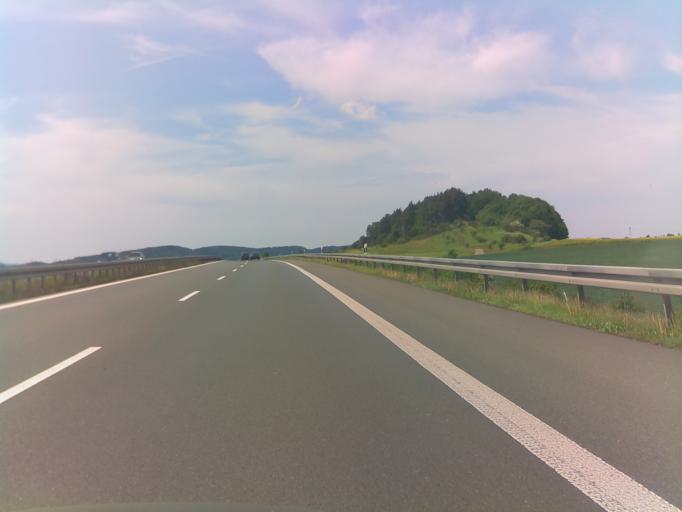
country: DE
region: Saxony-Anhalt
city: Westerhausen
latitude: 51.8157
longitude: 11.0869
